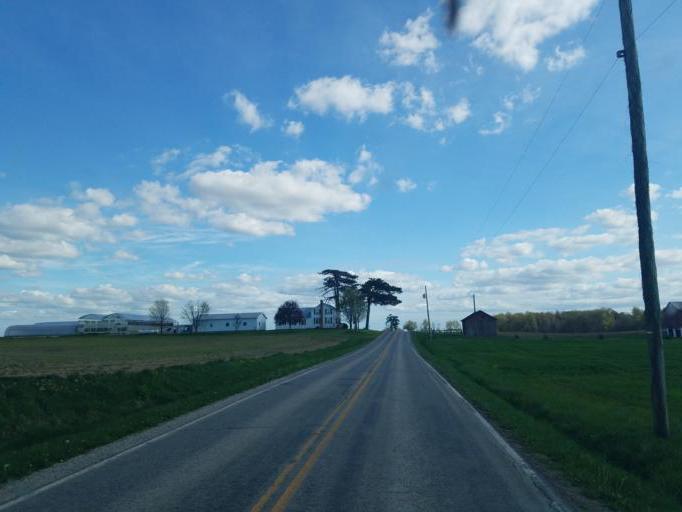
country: US
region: Ohio
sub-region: Huron County
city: Plymouth
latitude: 40.9581
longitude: -82.6505
